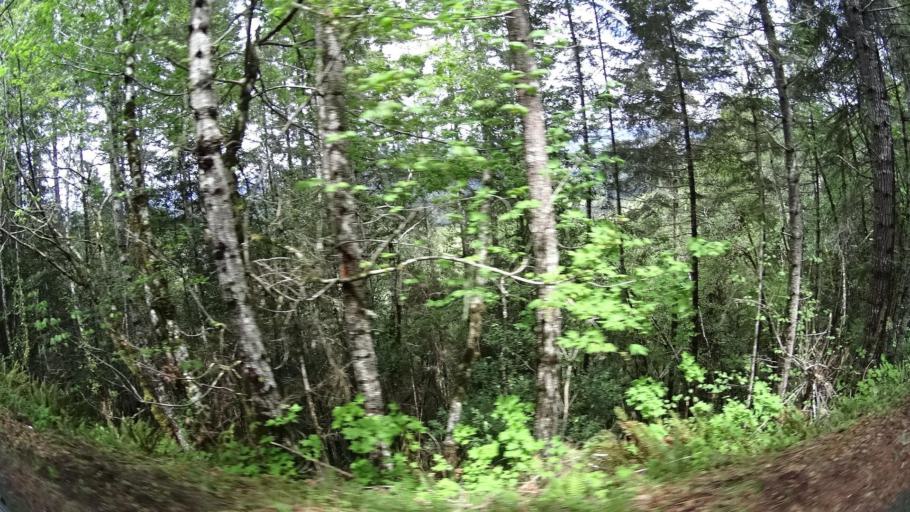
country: US
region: California
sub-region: Humboldt County
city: Blue Lake
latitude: 40.7596
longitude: -123.9110
